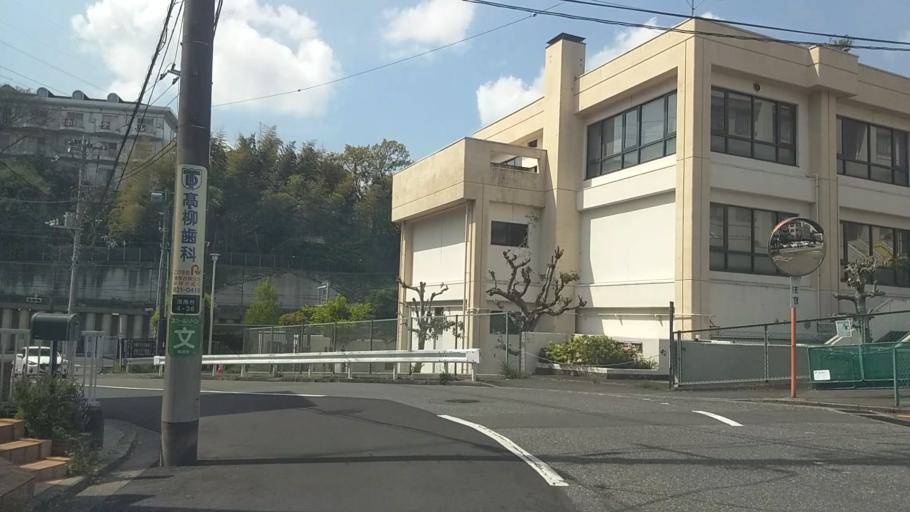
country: JP
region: Kanagawa
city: Kamakura
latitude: 35.3774
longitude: 139.5704
